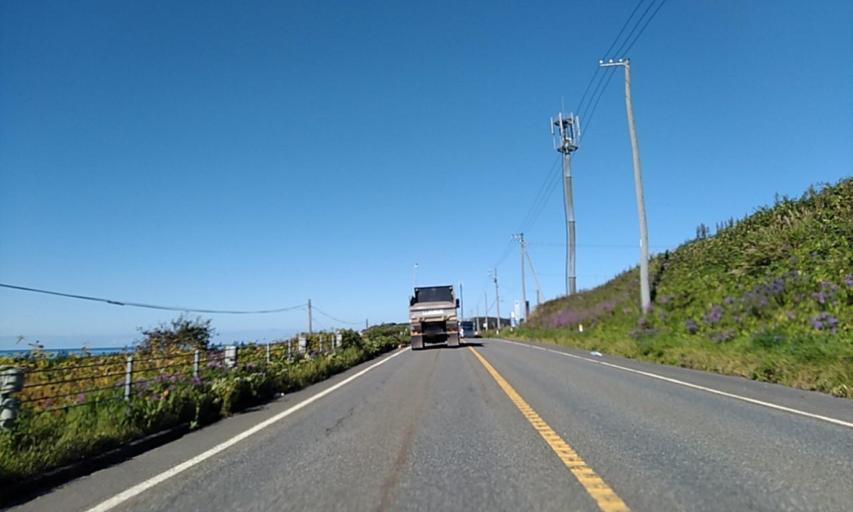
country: JP
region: Hokkaido
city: Shizunai-furukawacho
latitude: 42.4689
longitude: 142.1301
